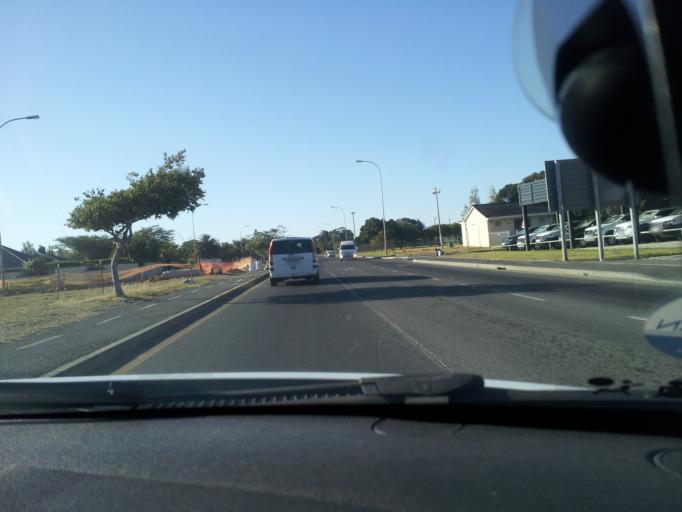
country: ZA
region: Western Cape
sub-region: Cape Winelands District Municipality
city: Stellenbosch
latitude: -34.1075
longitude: 18.8381
